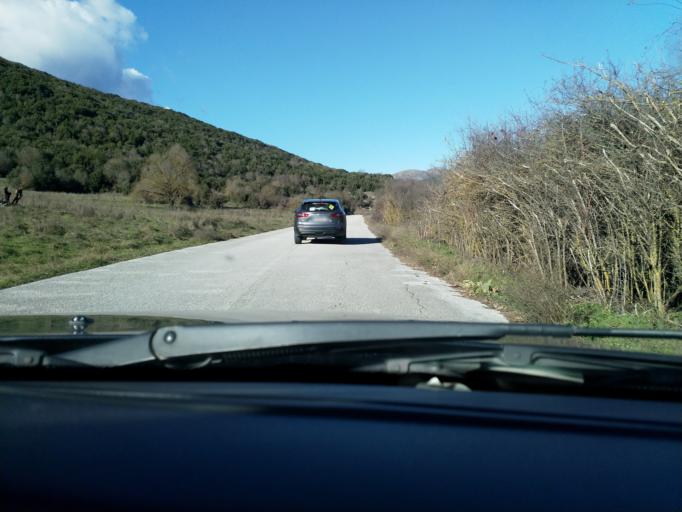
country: GR
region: Epirus
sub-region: Nomos Ioanninon
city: Kalpaki
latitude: 39.8844
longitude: 20.6737
